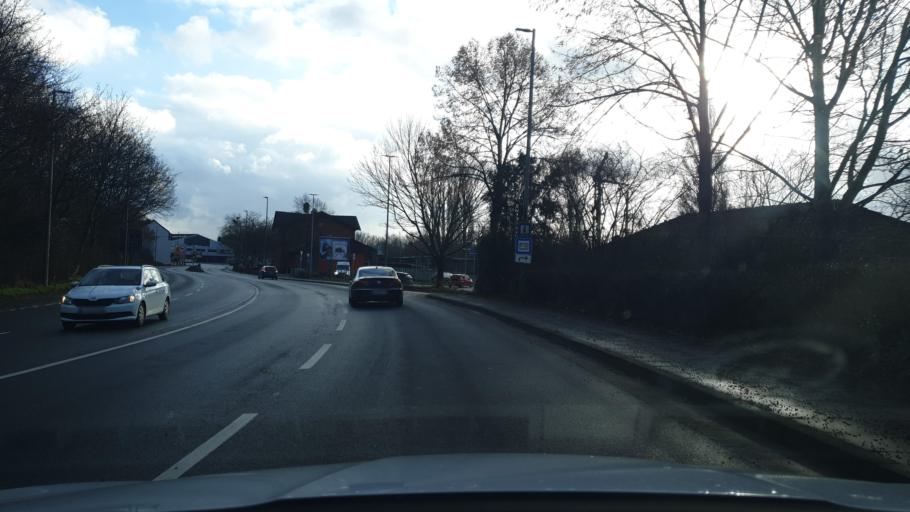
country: DE
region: North Rhine-Westphalia
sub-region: Regierungsbezirk Detmold
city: Bad Salzuflen
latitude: 52.0827
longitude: 8.7390
